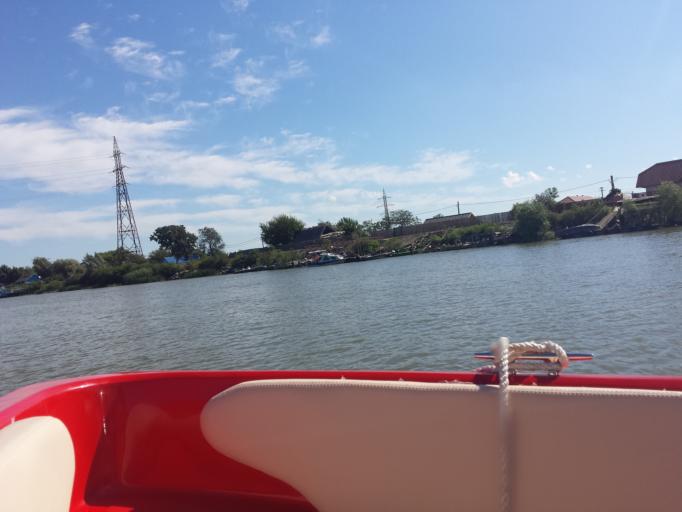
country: RO
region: Tulcea
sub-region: Comuna Crisan
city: Crisan
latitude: 45.2222
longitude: 29.2349
